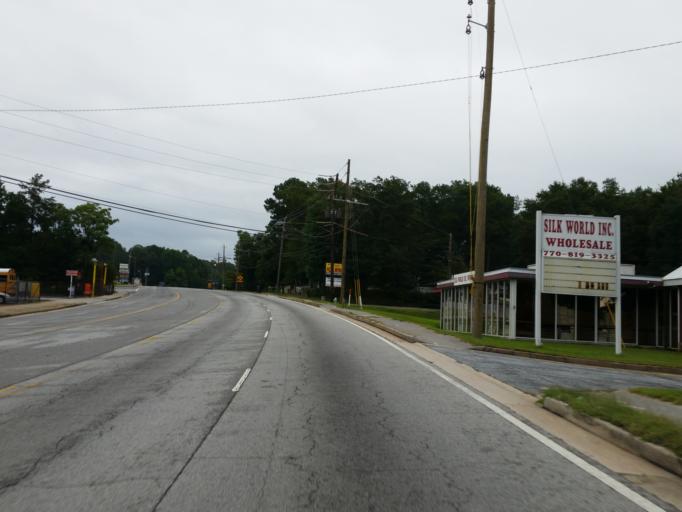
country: US
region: Georgia
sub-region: Cobb County
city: Austell
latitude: 33.8173
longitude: -84.6111
